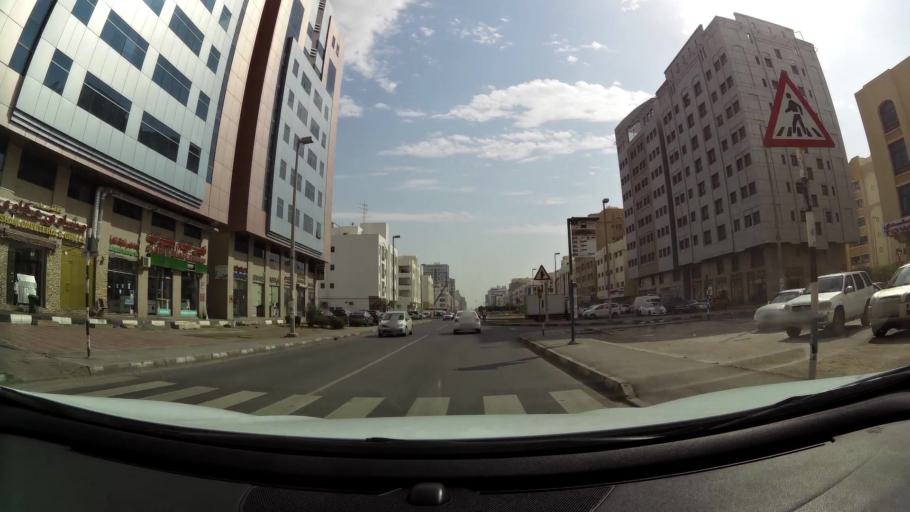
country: AE
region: Abu Dhabi
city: Abu Dhabi
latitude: 24.3333
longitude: 54.5348
